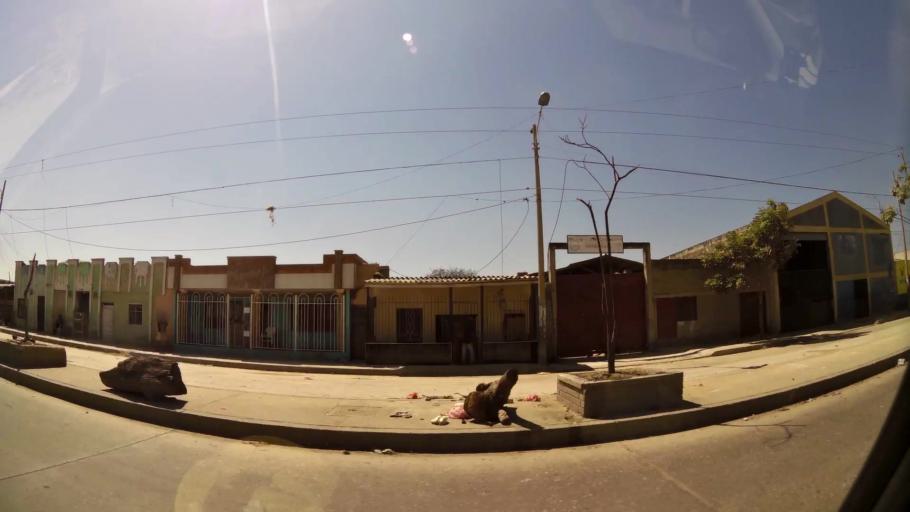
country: CO
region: Atlantico
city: Barranquilla
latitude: 10.9736
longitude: -74.7749
